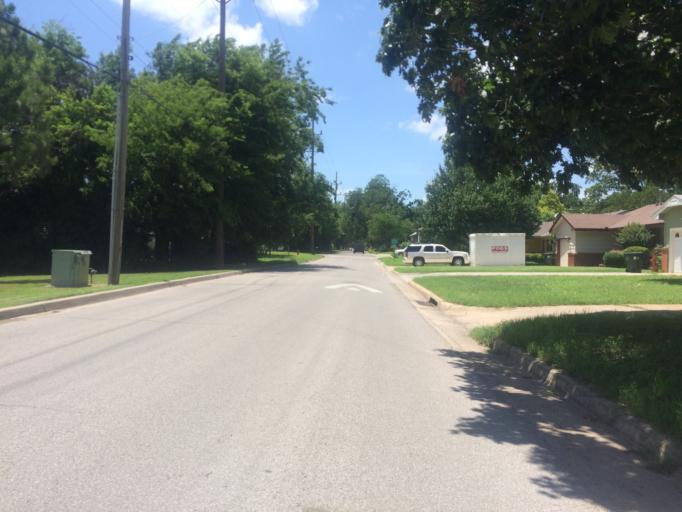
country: US
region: Oklahoma
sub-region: Cleveland County
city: Norman
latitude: 35.2148
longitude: -97.4537
